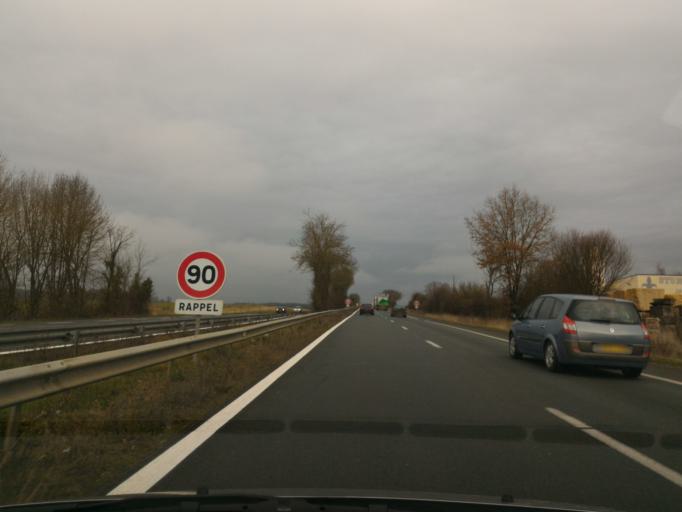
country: FR
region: Poitou-Charentes
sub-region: Departement de la Vienne
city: Vivonne
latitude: 46.4586
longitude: 0.2672
